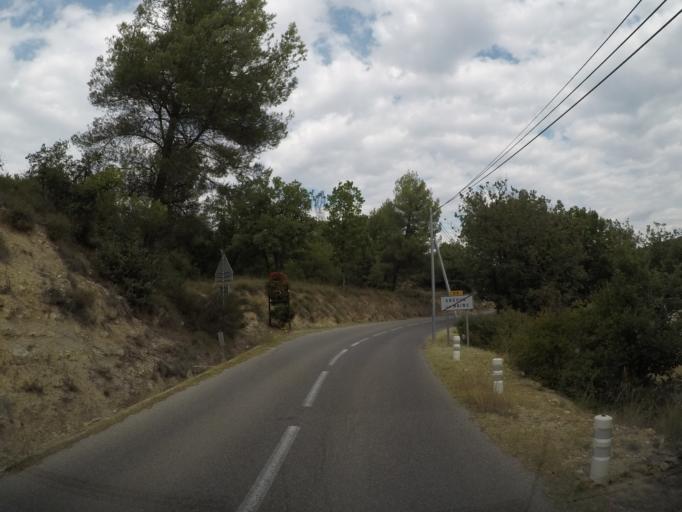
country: FR
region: Provence-Alpes-Cote d'Azur
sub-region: Departement des Alpes-de-Haute-Provence
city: Greoux-les-Bains
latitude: 43.7641
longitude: 5.8896
